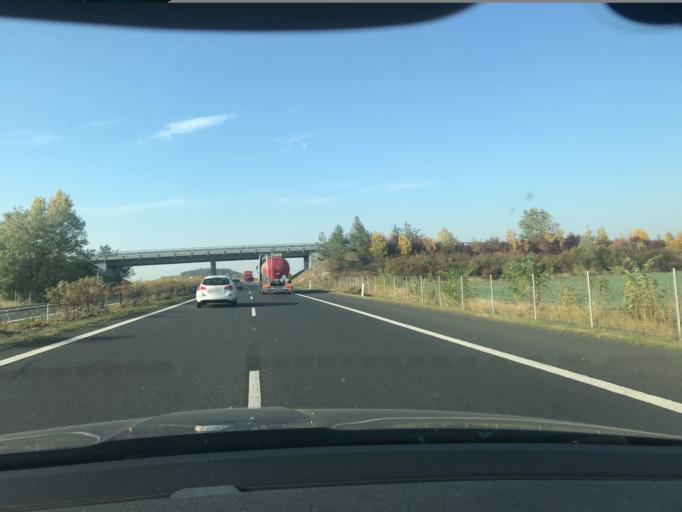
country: CZ
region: Ustecky
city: Roudnice nad Labem
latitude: 50.3550
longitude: 14.2736
